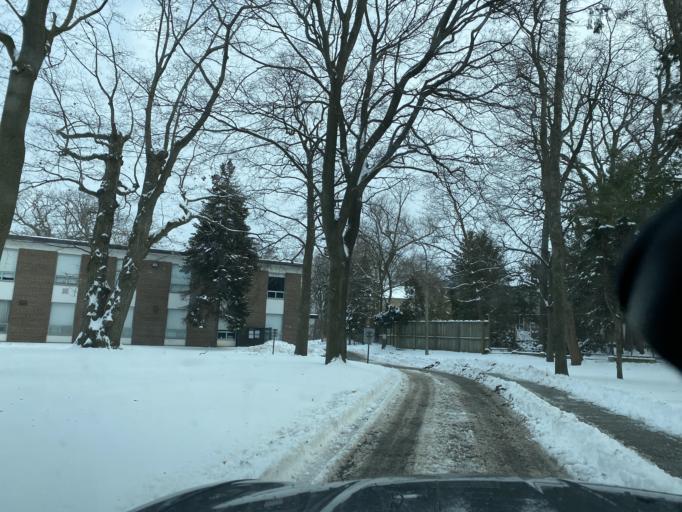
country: CA
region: Ontario
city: Toronto
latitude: 43.6737
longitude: -79.3669
